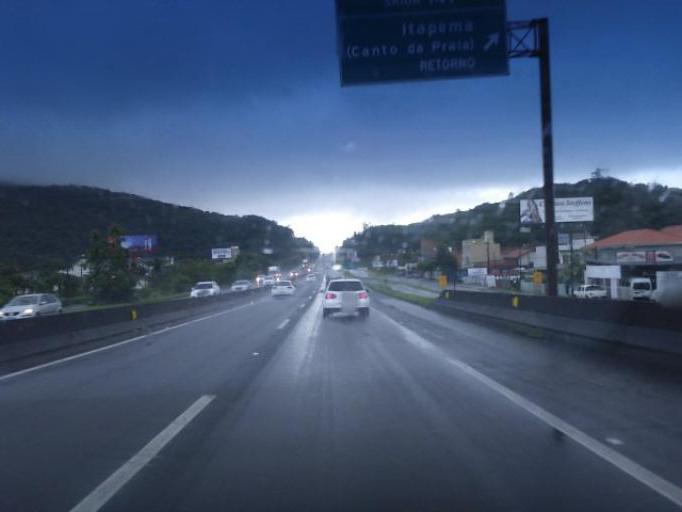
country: BR
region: Santa Catarina
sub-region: Itapema
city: Itapema
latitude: -27.0893
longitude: -48.6138
